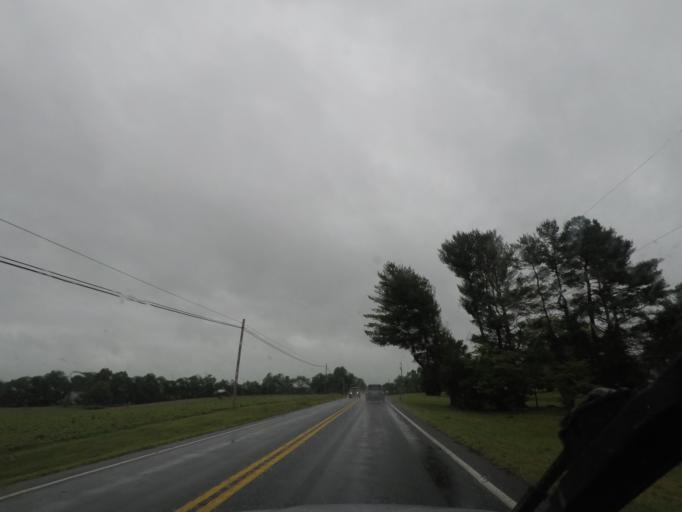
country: US
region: Virginia
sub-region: Orange County
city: Orange
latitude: 38.3064
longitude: -78.1325
